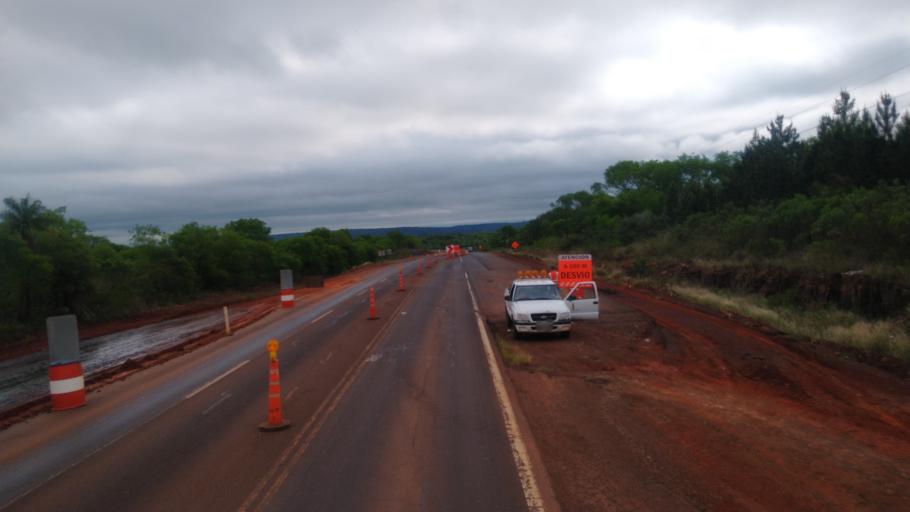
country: AR
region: Misiones
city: Santa Ana
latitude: -27.4113
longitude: -55.6093
